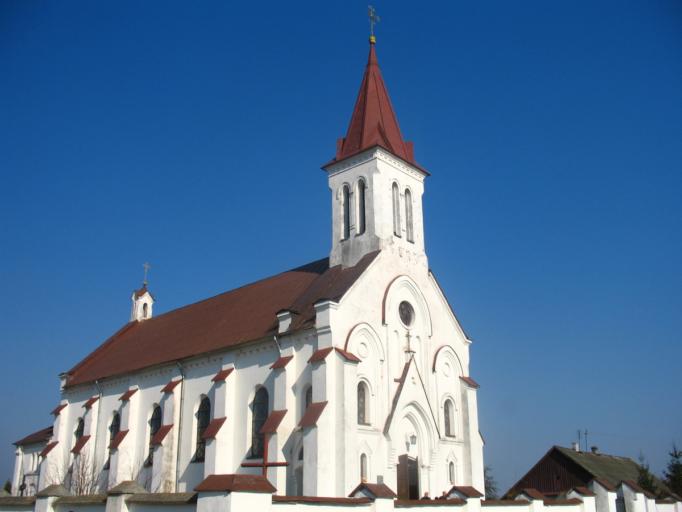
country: BY
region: Brest
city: Kosava
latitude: 52.7539
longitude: 25.1587
